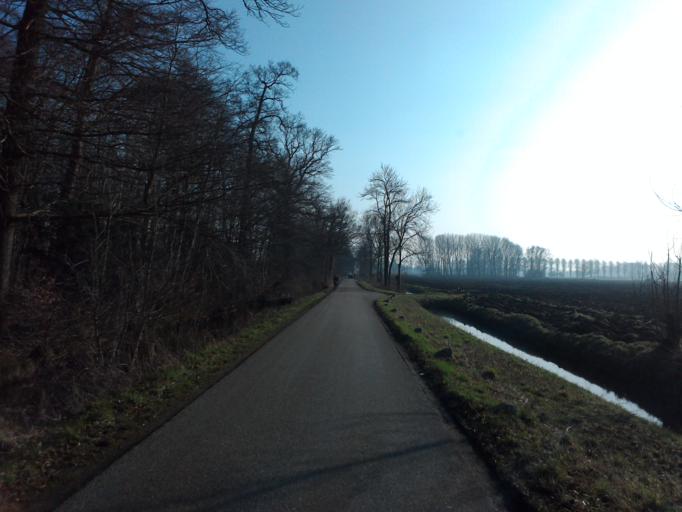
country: NL
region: Utrecht
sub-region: Gemeente De Bilt
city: De Bilt
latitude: 52.0883
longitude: 5.1887
